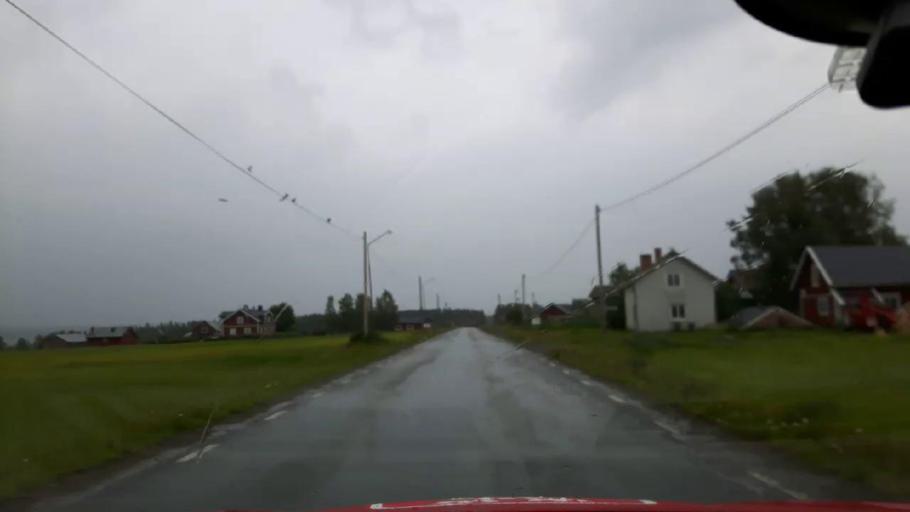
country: SE
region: Jaemtland
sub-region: OEstersunds Kommun
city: Brunflo
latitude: 62.9869
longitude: 14.8106
